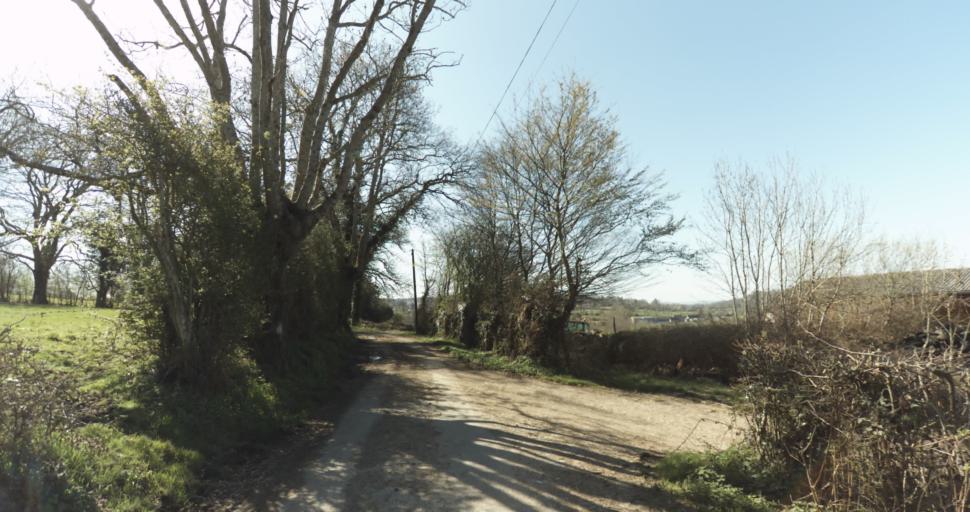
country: FR
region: Lower Normandy
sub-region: Departement du Calvados
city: Livarot
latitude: 48.9950
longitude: 0.0742
